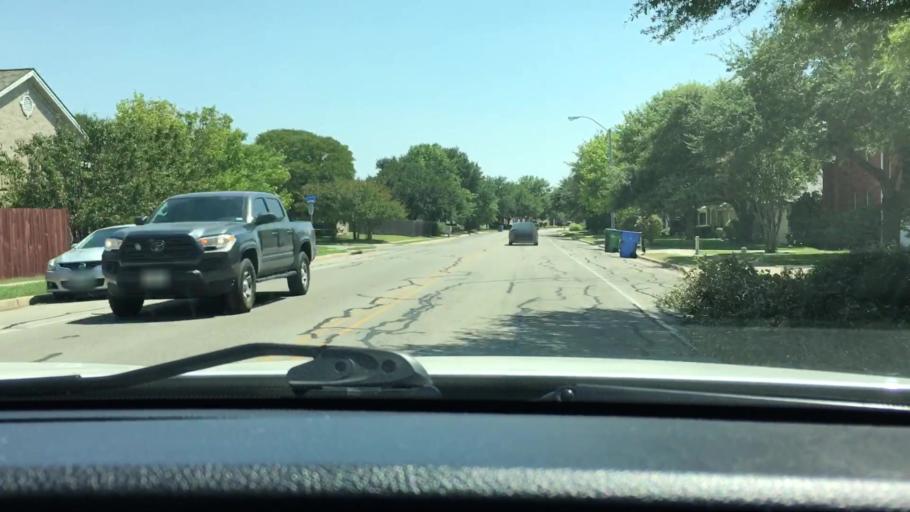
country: US
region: Texas
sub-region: Travis County
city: Windemere
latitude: 30.4692
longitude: -97.6536
